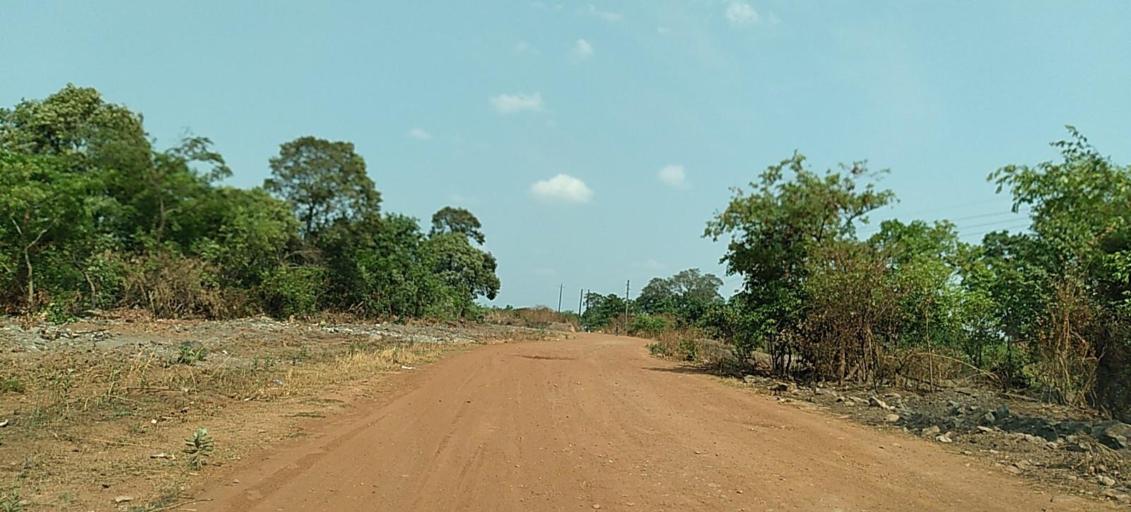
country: ZM
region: Copperbelt
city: Luanshya
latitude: -13.0930
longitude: 28.3089
